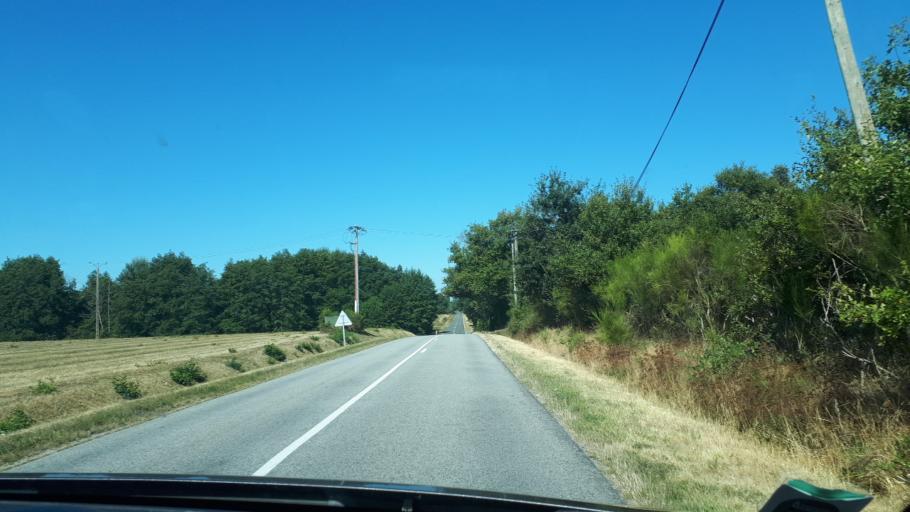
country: FR
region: Centre
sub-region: Departement du Loiret
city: Cerdon
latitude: 47.6367
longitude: 2.4197
